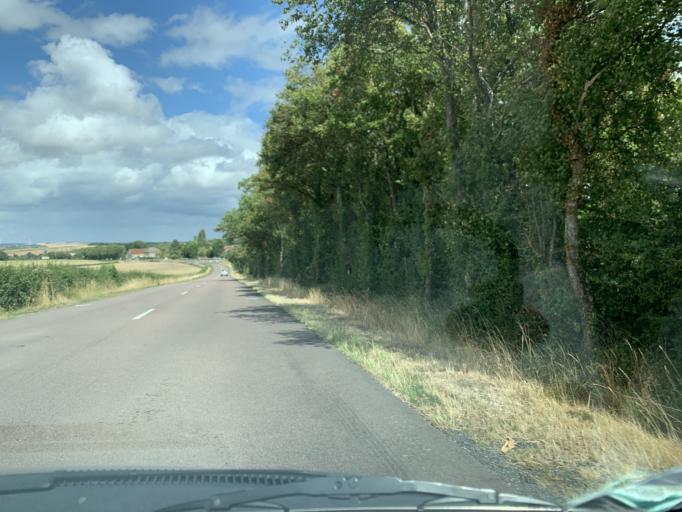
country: FR
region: Bourgogne
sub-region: Departement de la Nievre
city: Varzy
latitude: 47.3856
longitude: 3.4410
